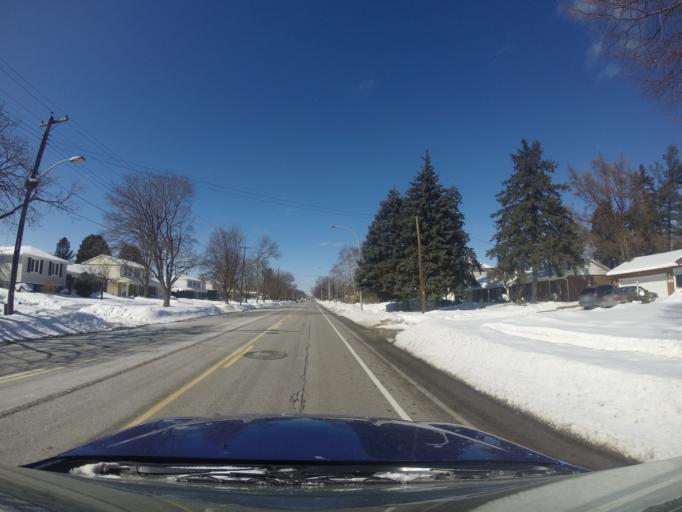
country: CA
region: Ontario
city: Burlington
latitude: 43.3504
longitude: -79.7663
